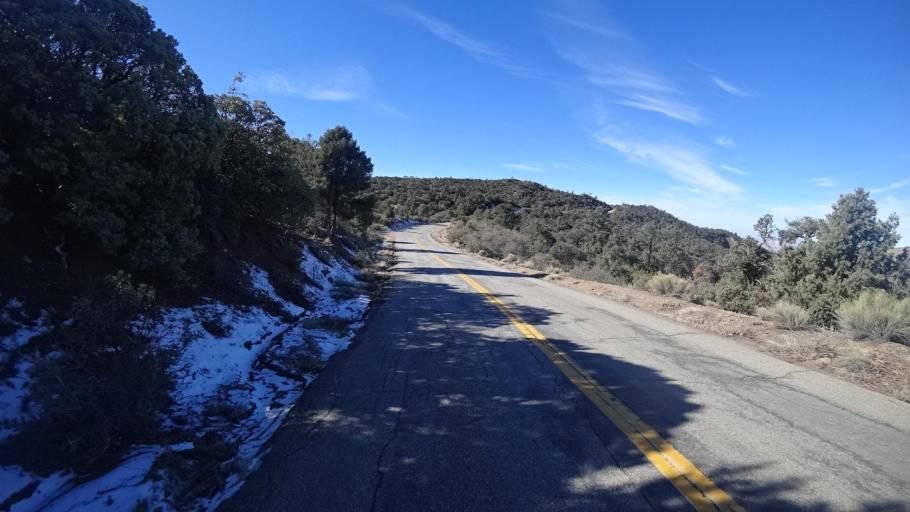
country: US
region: California
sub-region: Kern County
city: Pine Mountain Club
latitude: 34.8698
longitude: -119.2564
